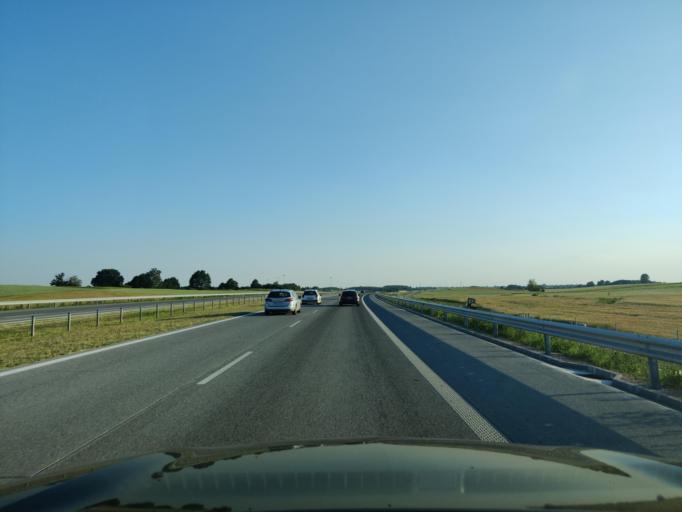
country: PL
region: Masovian Voivodeship
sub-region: Powiat mlawski
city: Mlawa
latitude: 53.0885
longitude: 20.4054
